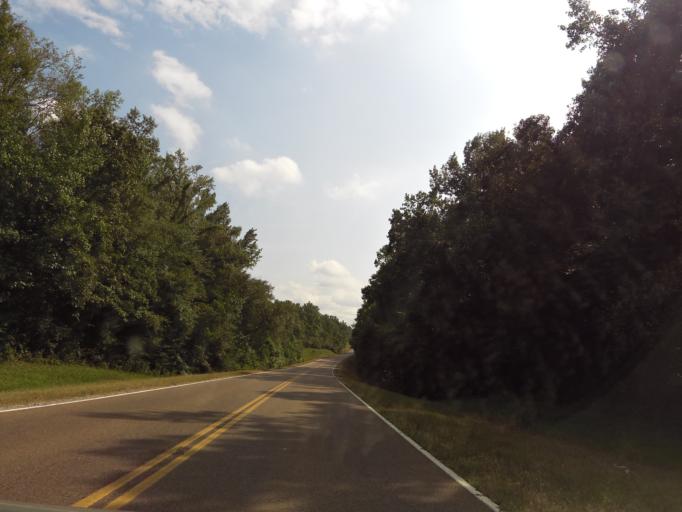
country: US
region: Tennessee
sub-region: Hardin County
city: Crump
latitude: 35.1316
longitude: -88.3610
